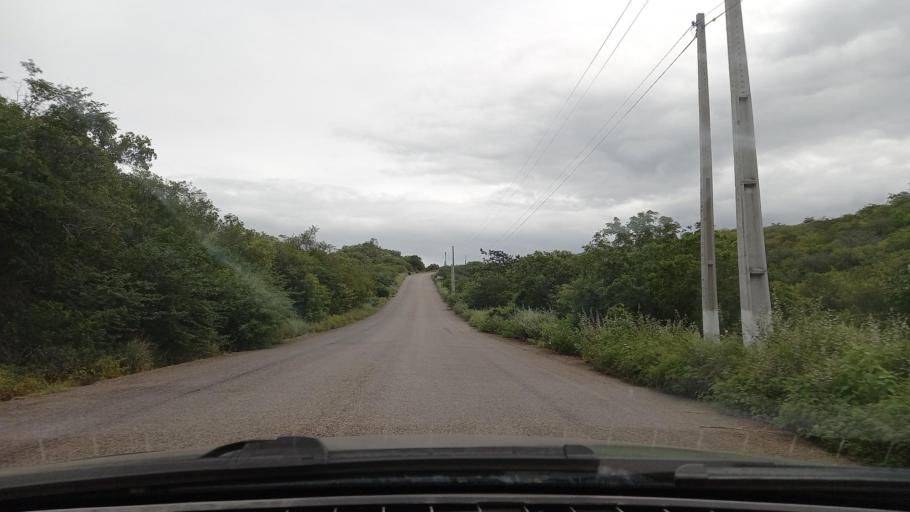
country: BR
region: Sergipe
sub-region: Caninde De Sao Francisco
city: Caninde de Sao Francisco
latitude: -9.6321
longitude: -37.7818
